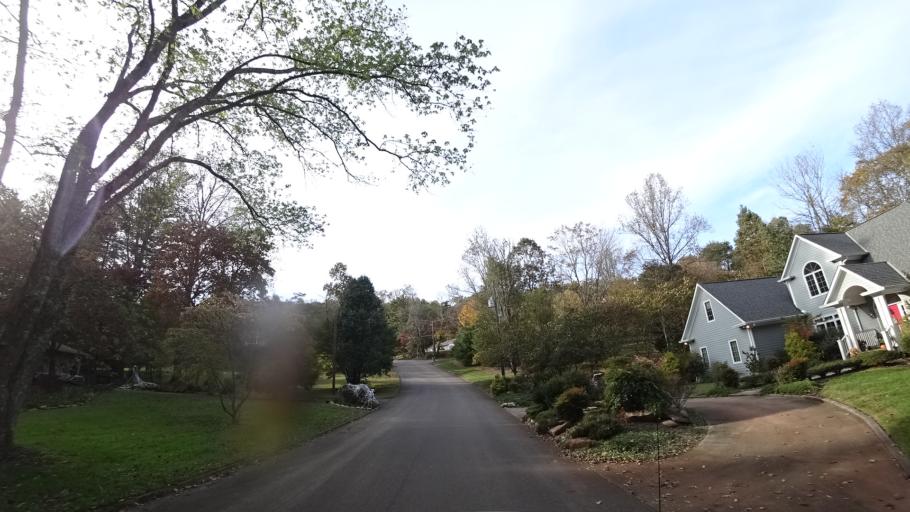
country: US
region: Tennessee
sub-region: Knox County
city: Knoxville
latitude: 35.9107
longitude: -83.9885
